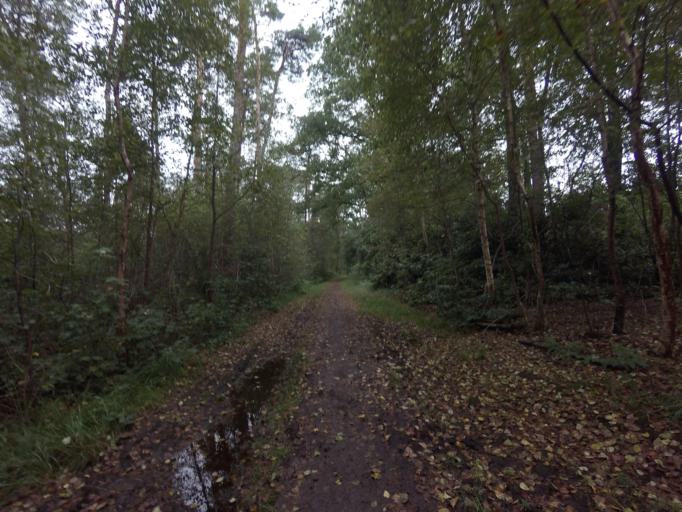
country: NL
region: Gelderland
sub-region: Gemeente Lochem
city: Harfsen
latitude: 52.2789
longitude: 6.2829
